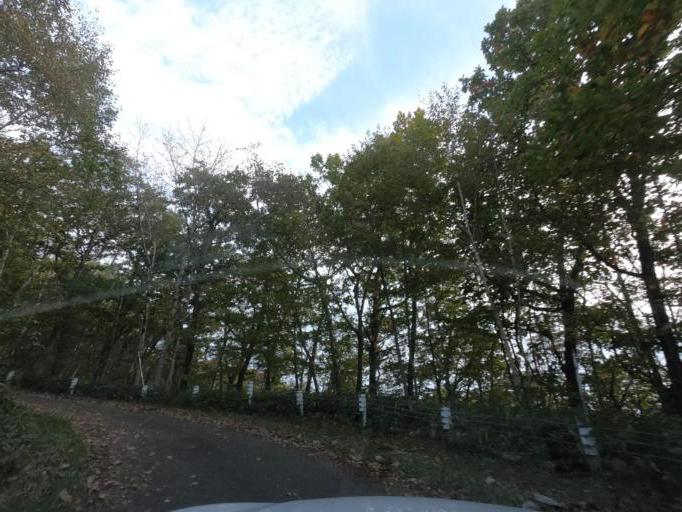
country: JP
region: Hokkaido
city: Obihiro
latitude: 42.5853
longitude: 143.3116
